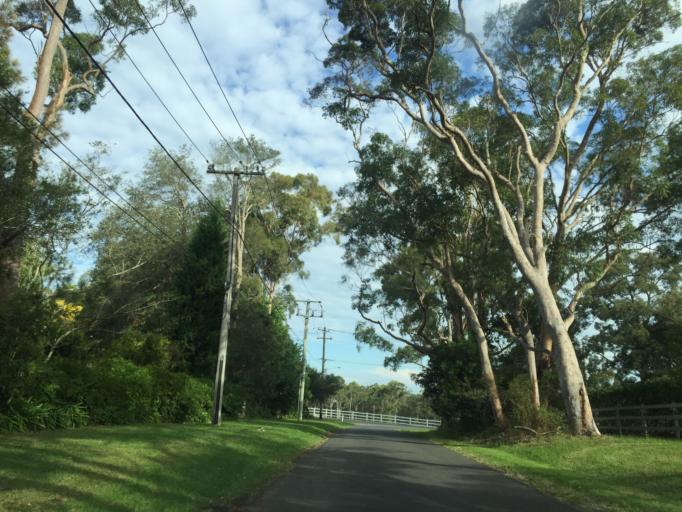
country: AU
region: New South Wales
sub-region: Hornsby Shire
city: Galston
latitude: -33.6461
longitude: 151.0752
